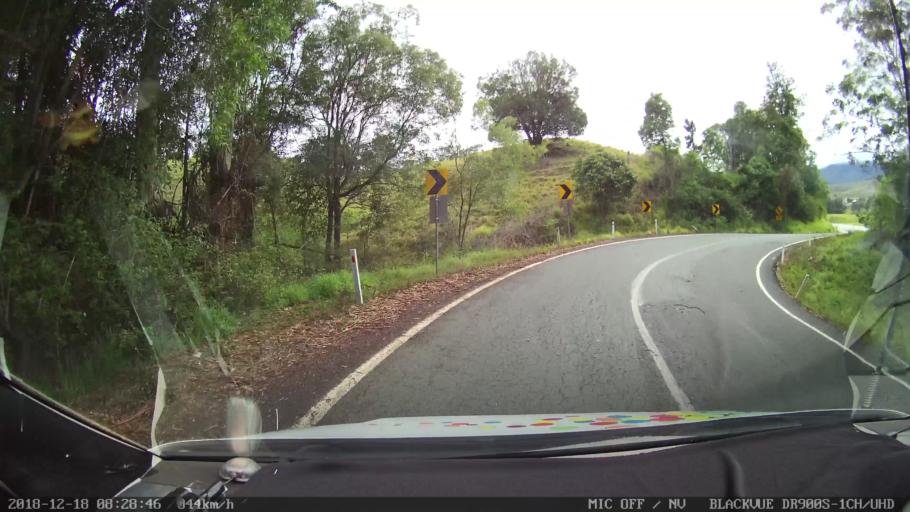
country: AU
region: New South Wales
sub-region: Kyogle
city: Kyogle
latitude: -28.3256
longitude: 152.7553
